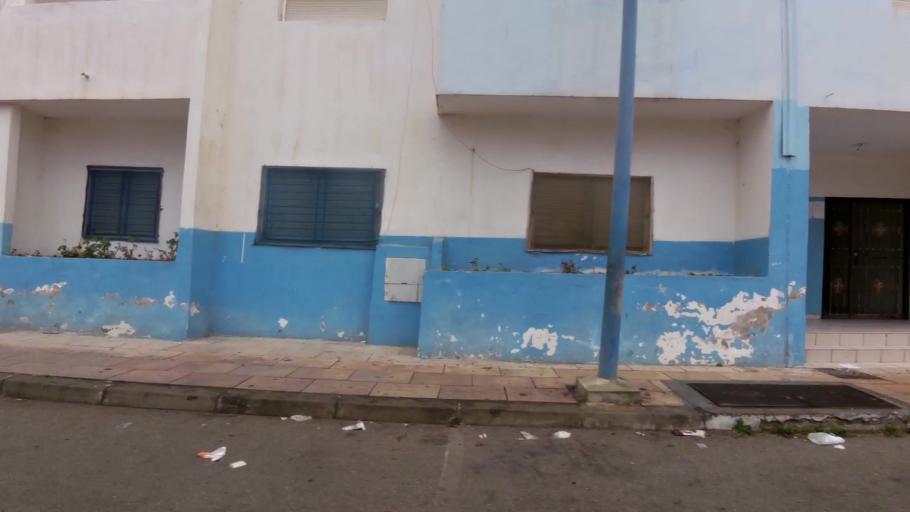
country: MA
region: Tanger-Tetouan
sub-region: Tetouan
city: Martil
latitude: 35.6164
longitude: -5.2822
